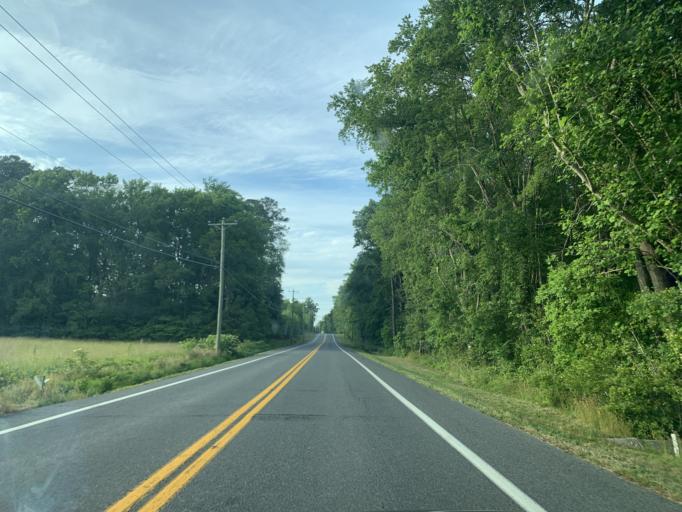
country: US
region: Maryland
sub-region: Worcester County
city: Snow Hill
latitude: 38.0833
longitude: -75.3984
